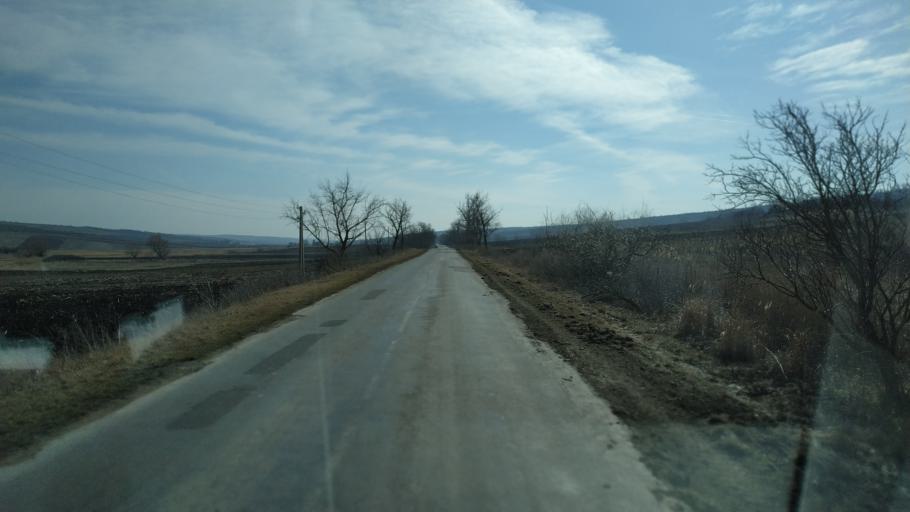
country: MD
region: Nisporeni
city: Nisporeni
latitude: 47.1176
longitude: 28.1221
